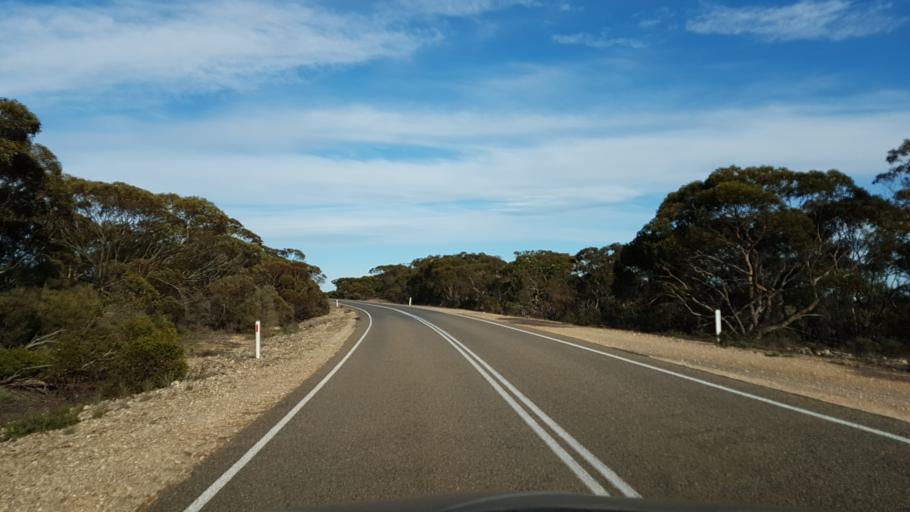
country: AU
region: South Australia
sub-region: Mid Murray
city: Mannum
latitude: -35.0080
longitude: 139.5259
